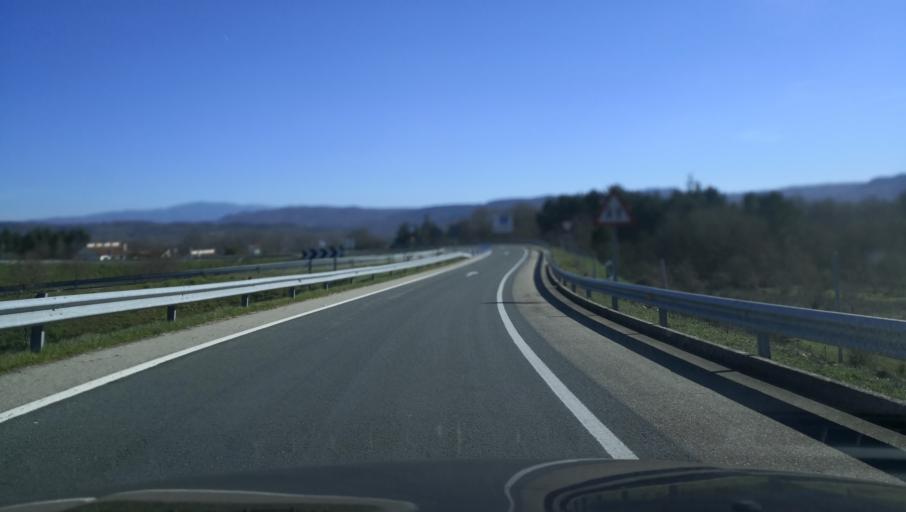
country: ES
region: Galicia
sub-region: Provincia de Ourense
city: Allariz
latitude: 42.2072
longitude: -7.8196
